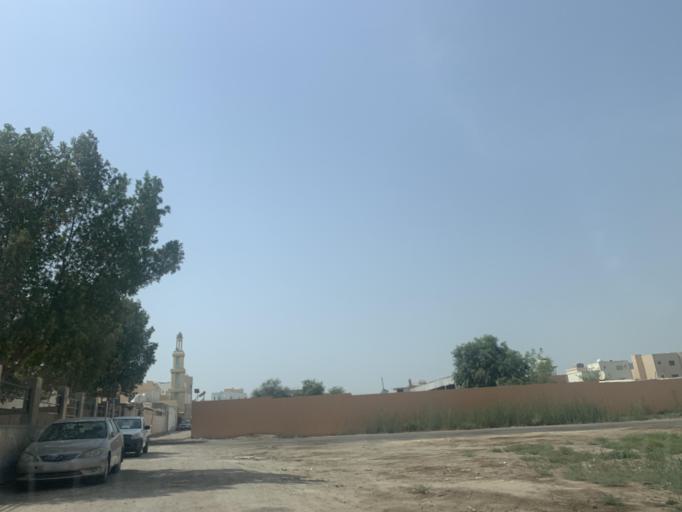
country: BH
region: Northern
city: Madinat `Isa
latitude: 26.1920
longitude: 50.4908
